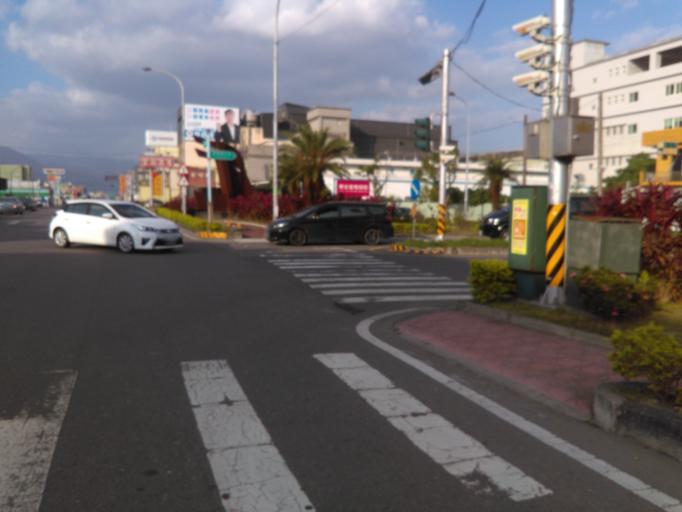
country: TW
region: Taiwan
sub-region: Yilan
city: Yilan
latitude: 24.7721
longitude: 121.7575
